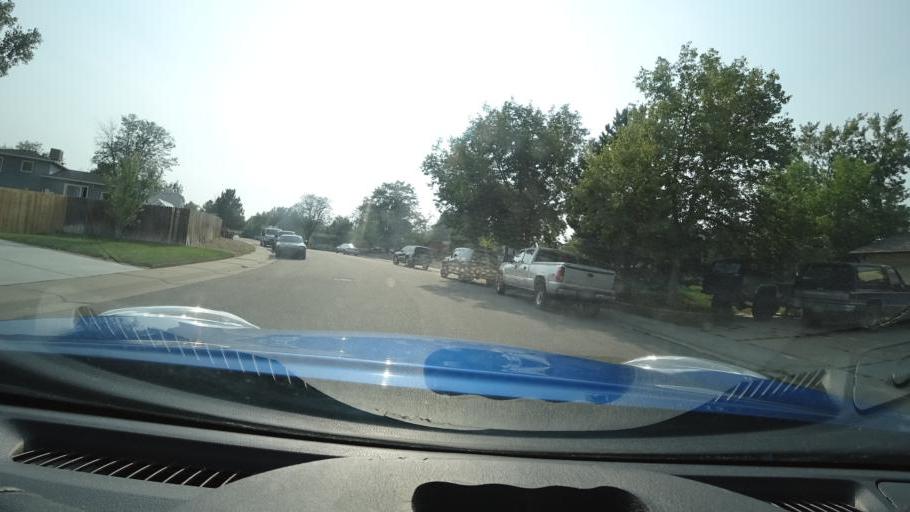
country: US
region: Colorado
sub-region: Adams County
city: Aurora
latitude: 39.6669
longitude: -104.7972
